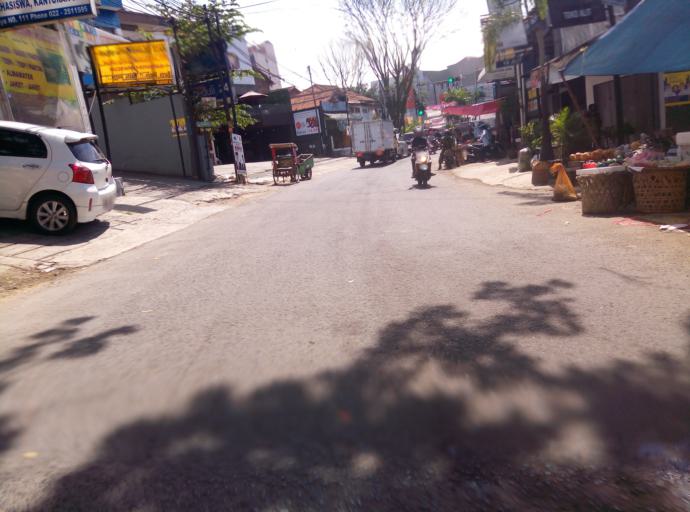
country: ID
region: West Java
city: Bandung
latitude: -6.9006
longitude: 107.6437
